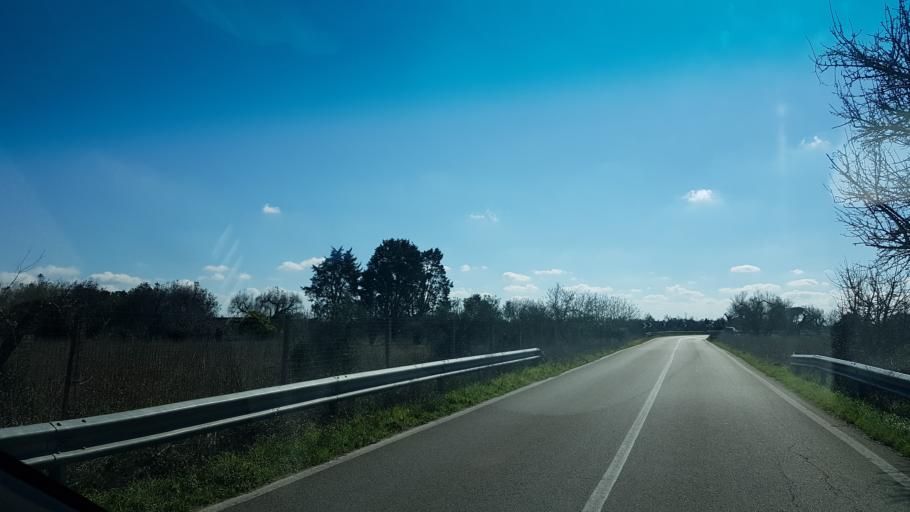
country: IT
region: Apulia
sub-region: Provincia di Brindisi
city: Cellino San Marco
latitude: 40.4396
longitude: 17.9890
